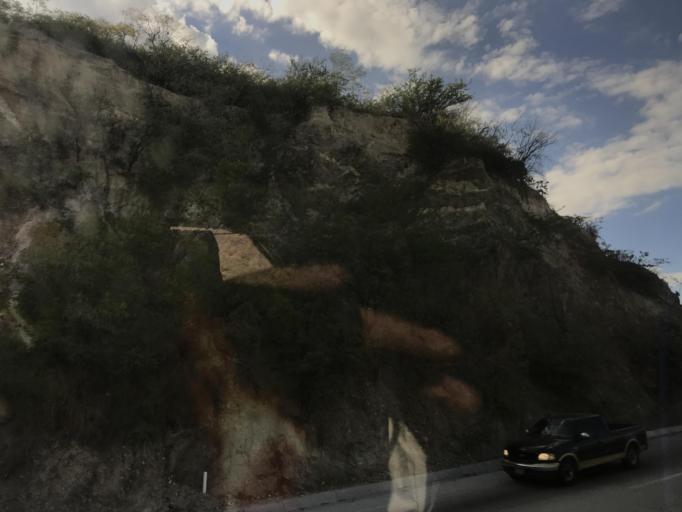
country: GT
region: El Progreso
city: Guastatoya
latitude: 14.8488
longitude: -90.1177
